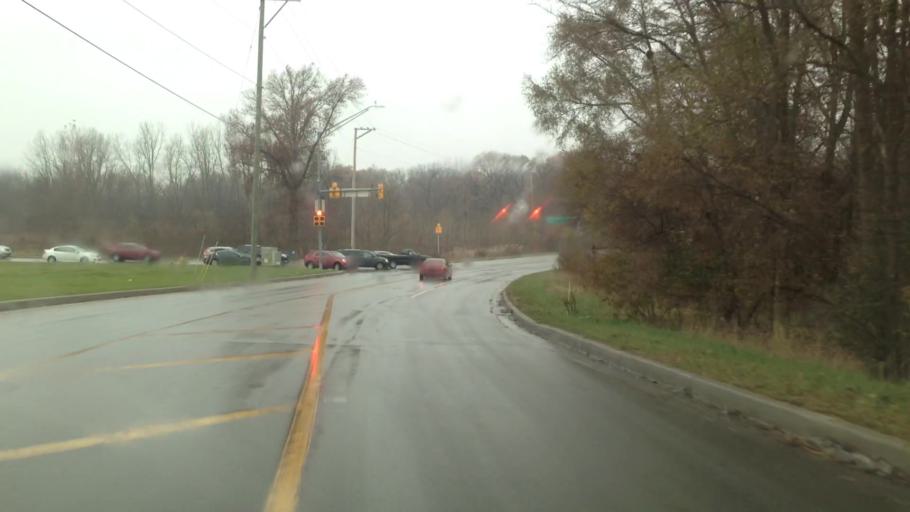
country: US
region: Indiana
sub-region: Saint Joseph County
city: Mishawaka
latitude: 41.7209
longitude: -86.1635
